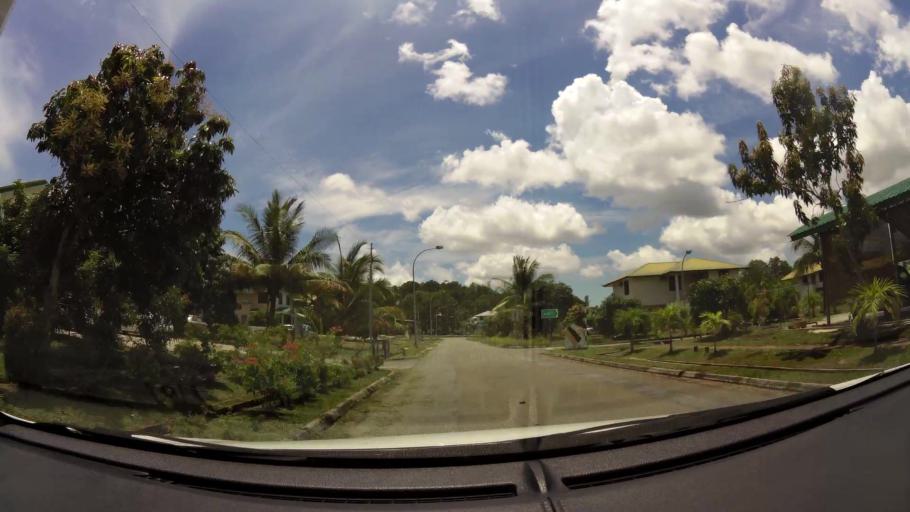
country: BN
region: Brunei and Muara
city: Bandar Seri Begawan
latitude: 4.9597
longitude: 114.9167
